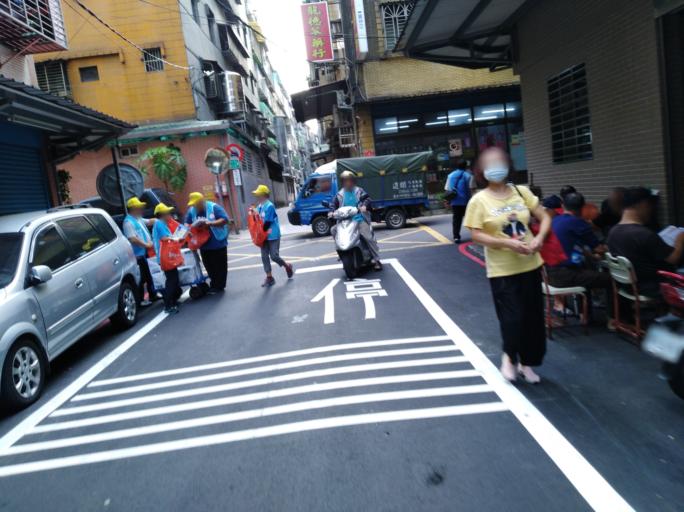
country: TW
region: Taipei
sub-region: Taipei
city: Banqiao
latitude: 25.0396
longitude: 121.4252
